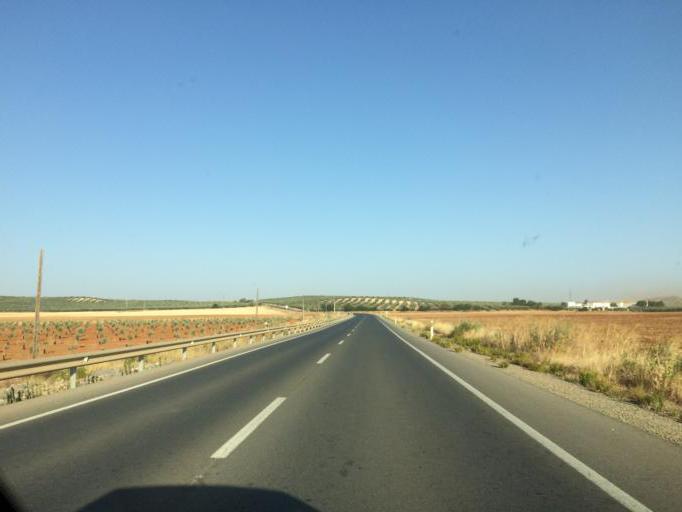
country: ES
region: Andalusia
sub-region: Provincia de Malaga
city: Humilladero
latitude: 37.0528
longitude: -4.7599
